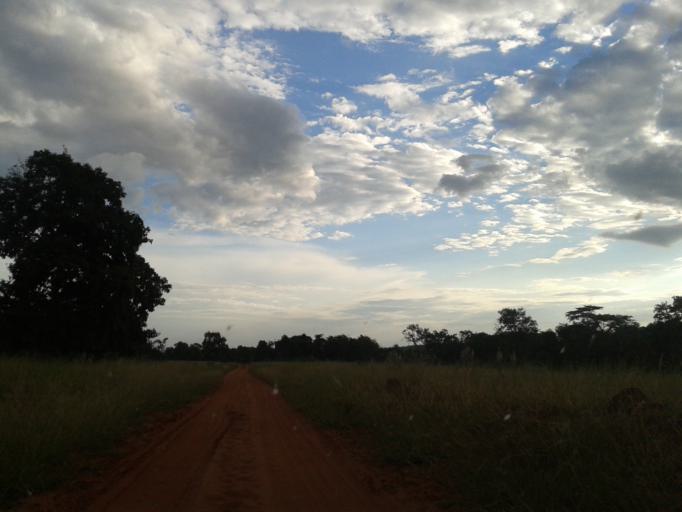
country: BR
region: Minas Gerais
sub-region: Campina Verde
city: Campina Verde
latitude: -19.3425
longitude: -49.6594
